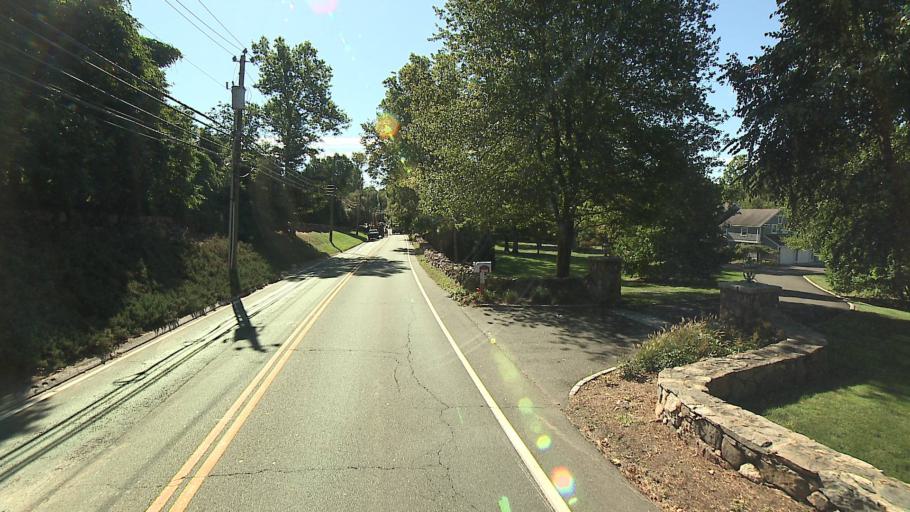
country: US
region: Connecticut
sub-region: Fairfield County
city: Darien
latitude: 41.0991
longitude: -73.4814
